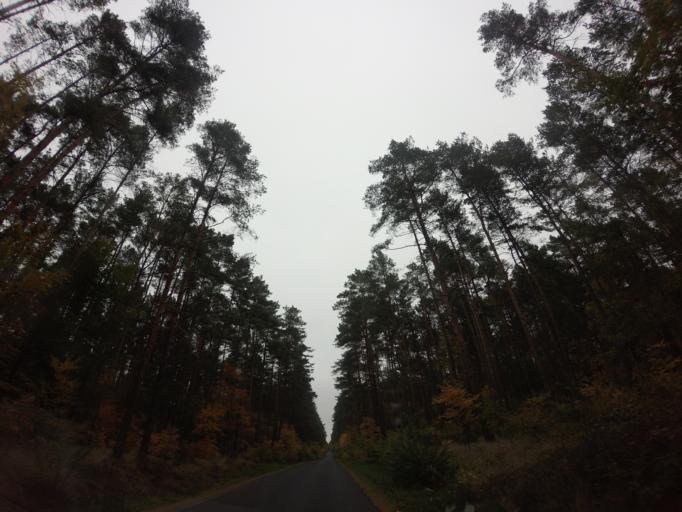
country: PL
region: West Pomeranian Voivodeship
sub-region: Powiat choszczenski
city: Bierzwnik
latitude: 53.1316
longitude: 15.6653
